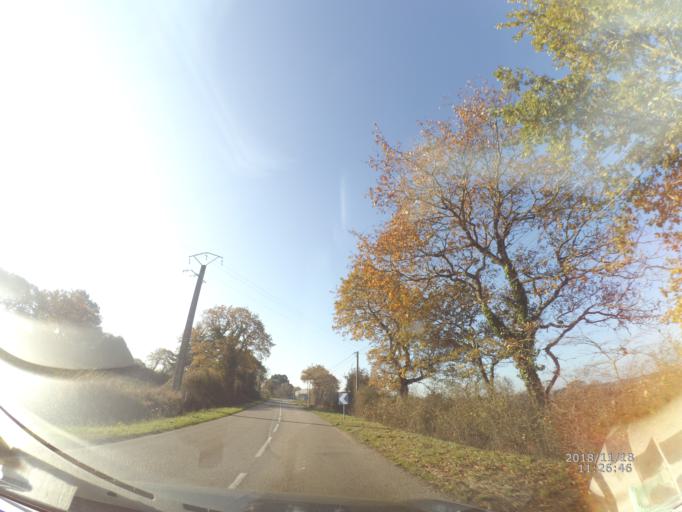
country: FR
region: Pays de la Loire
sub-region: Departement de la Loire-Atlantique
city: Saint-Brevin-les-Pins
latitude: 47.2219
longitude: -2.1350
